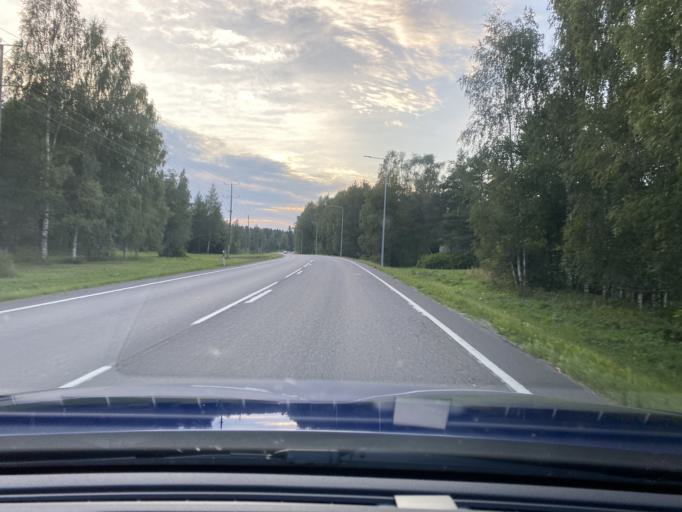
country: FI
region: Satakunta
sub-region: Pohjois-Satakunta
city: Kankaanpaeae
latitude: 61.8035
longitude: 22.3875
